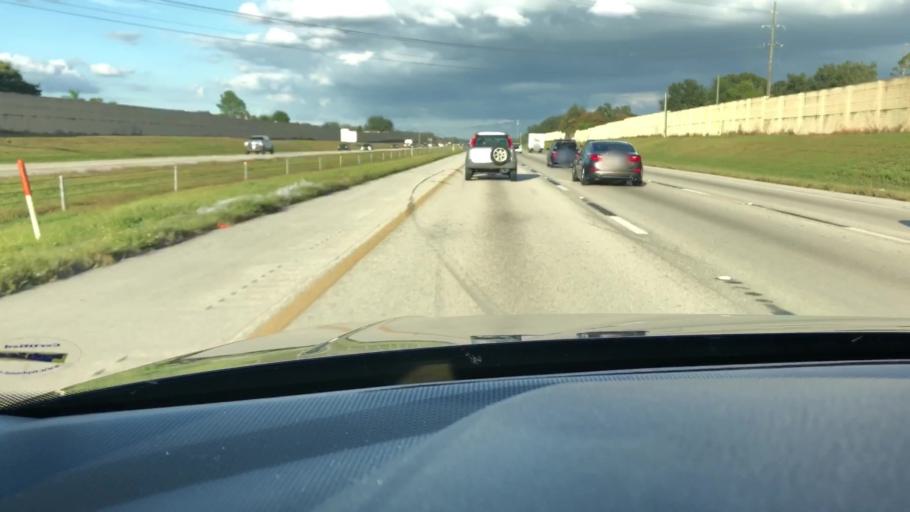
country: US
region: Florida
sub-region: Polk County
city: Gibsonia
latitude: 28.1174
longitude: -81.9361
